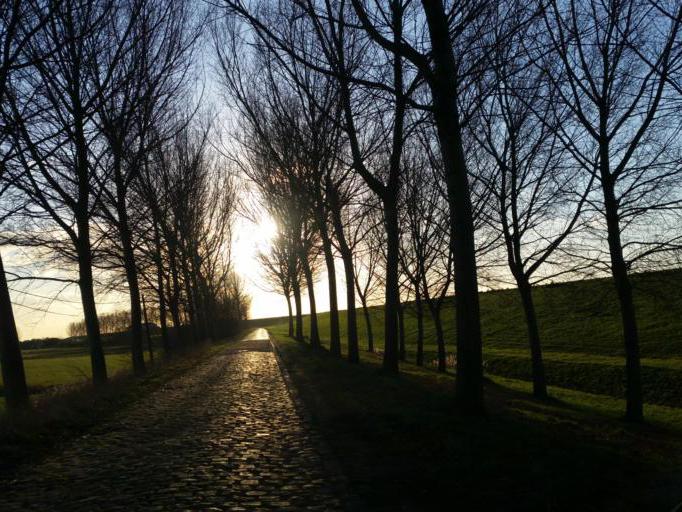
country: NL
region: North Brabant
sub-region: Gemeente Woensdrecht
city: Woensdrecht
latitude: 51.3325
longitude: 4.2322
